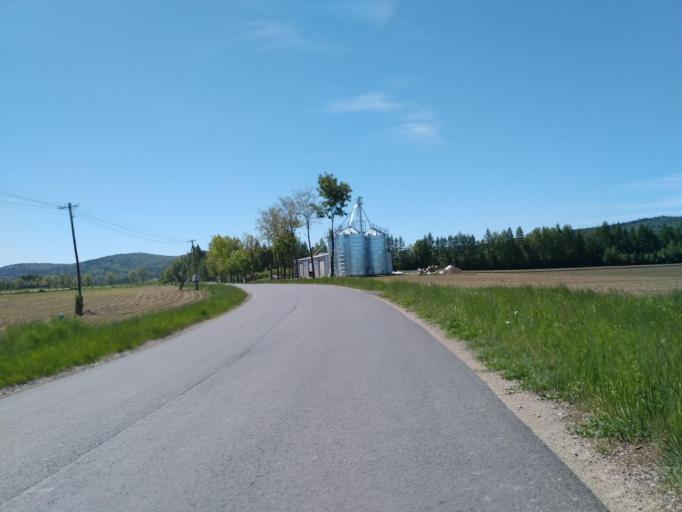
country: PL
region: Subcarpathian Voivodeship
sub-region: Powiat krosnienski
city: Sieniawa
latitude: 49.5581
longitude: 21.9362
